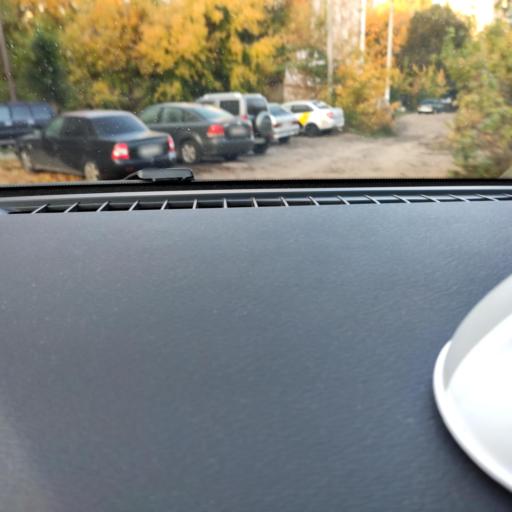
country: RU
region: Samara
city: Petra-Dubrava
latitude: 53.2519
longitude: 50.2613
